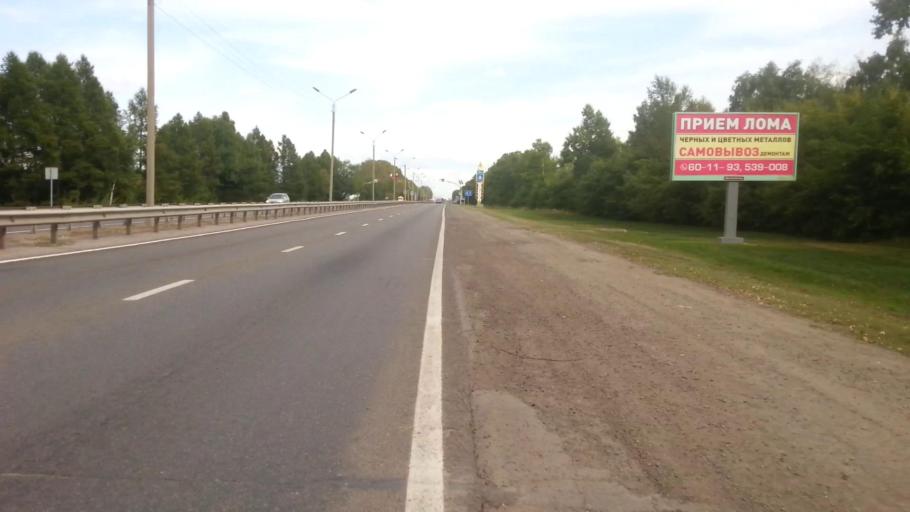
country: RU
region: Altai Krai
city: Vlasikha
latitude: 53.3529
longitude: 83.5641
